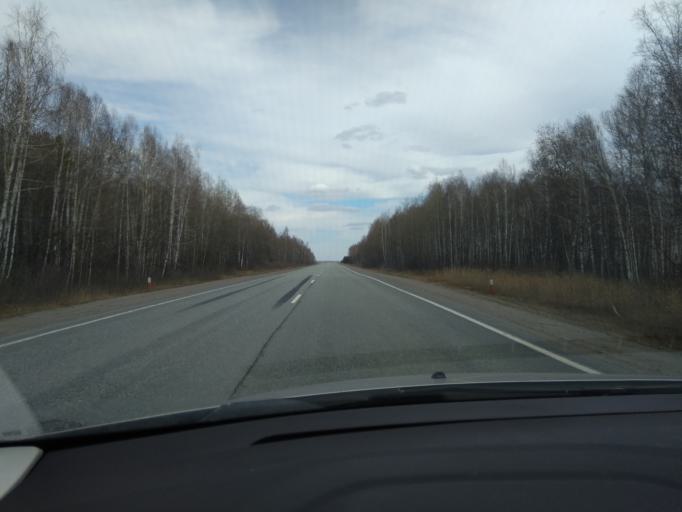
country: RU
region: Sverdlovsk
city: Yelanskiy
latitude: 56.7668
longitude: 62.4260
